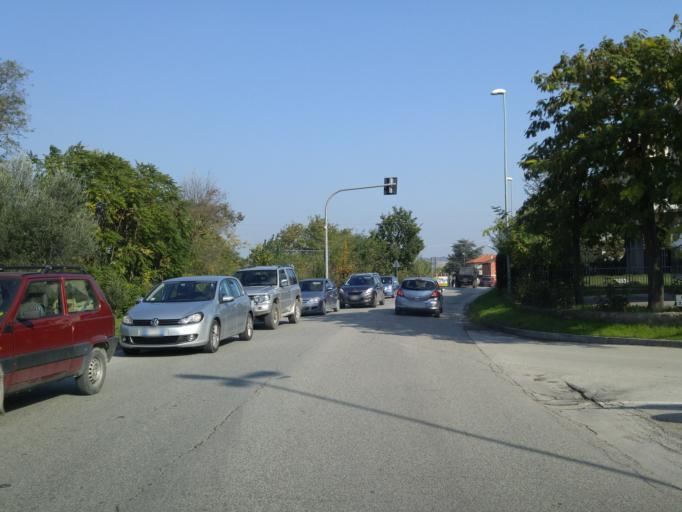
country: IT
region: The Marches
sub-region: Provincia di Pesaro e Urbino
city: Lucrezia
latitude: 43.7779
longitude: 12.9405
